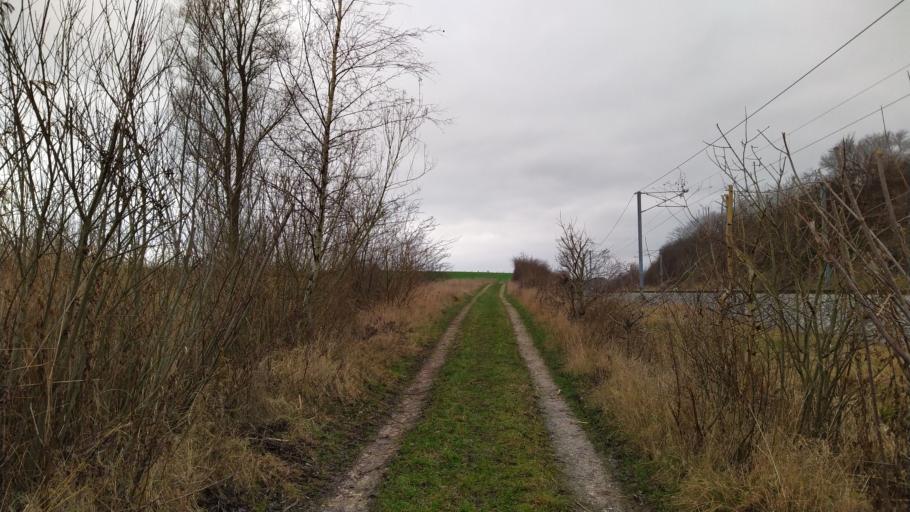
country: DK
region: Capital Region
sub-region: Egedal Kommune
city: Vekso
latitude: 55.7503
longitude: 12.2350
